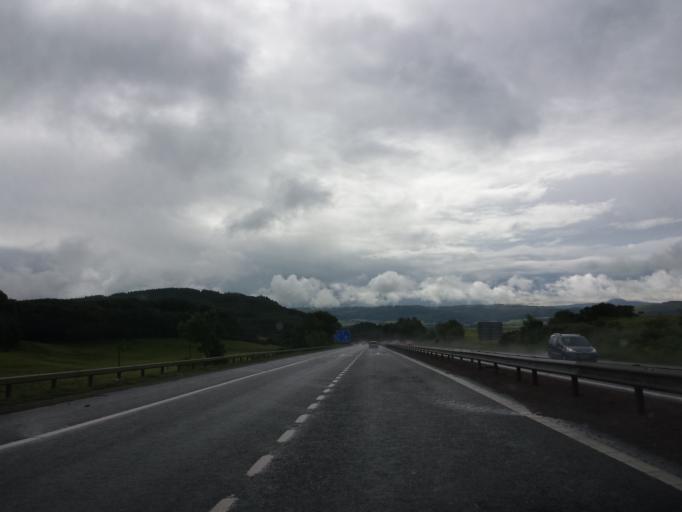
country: GB
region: Scotland
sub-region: Perth and Kinross
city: Perth
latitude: 56.3716
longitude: -3.4397
